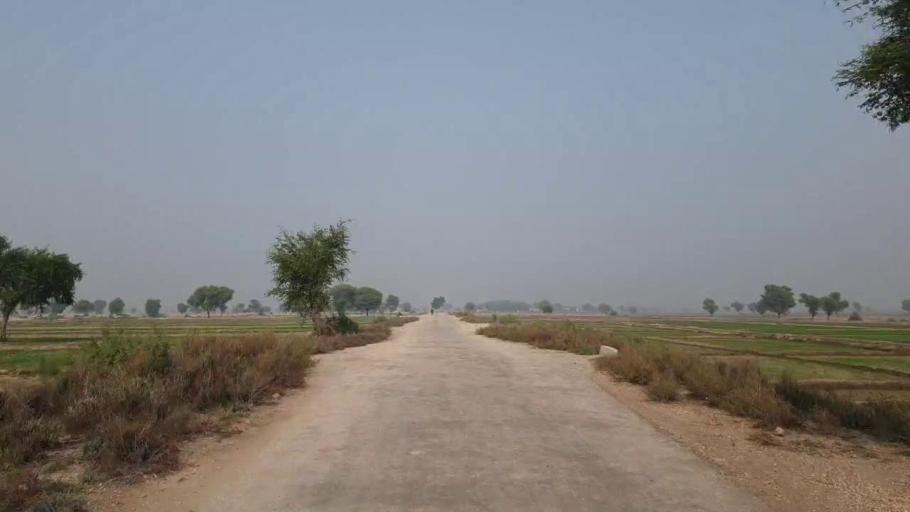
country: PK
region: Sindh
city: Bhan
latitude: 26.5157
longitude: 67.6897
